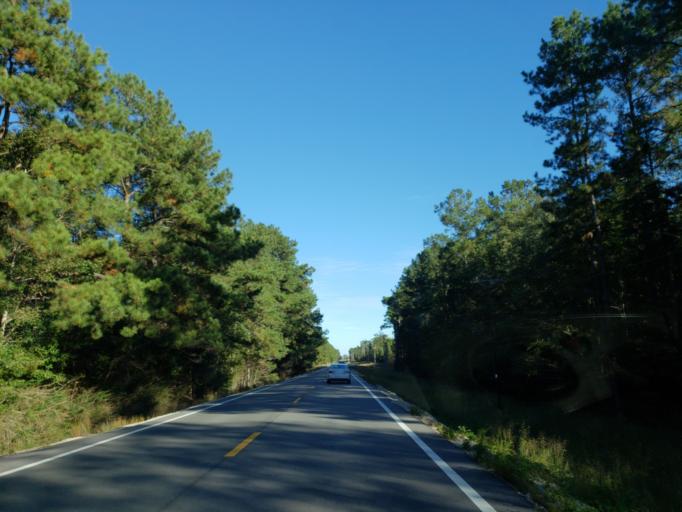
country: US
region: Mississippi
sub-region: Perry County
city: Richton
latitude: 31.3651
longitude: -89.0555
